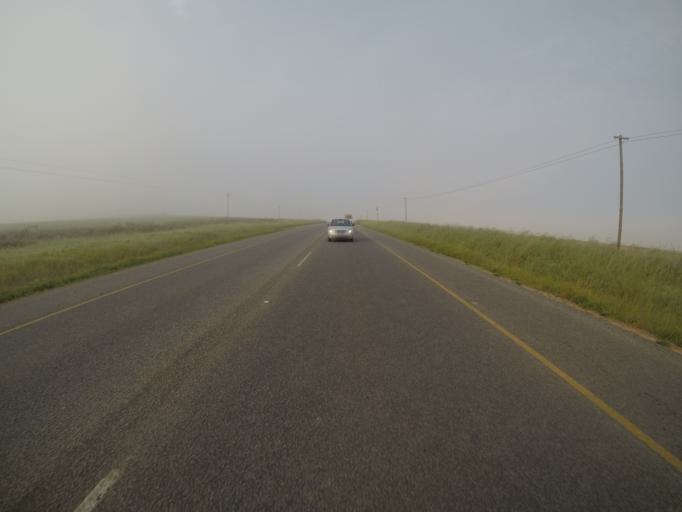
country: ZA
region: Western Cape
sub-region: West Coast District Municipality
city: Malmesbury
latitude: -33.6494
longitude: 18.7111
